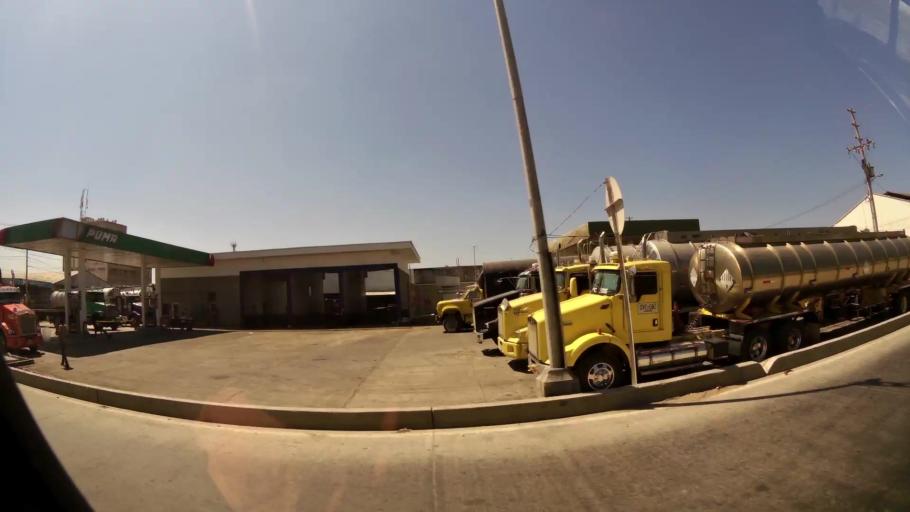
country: CO
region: Atlantico
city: Barranquilla
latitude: 10.9819
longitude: -74.7698
